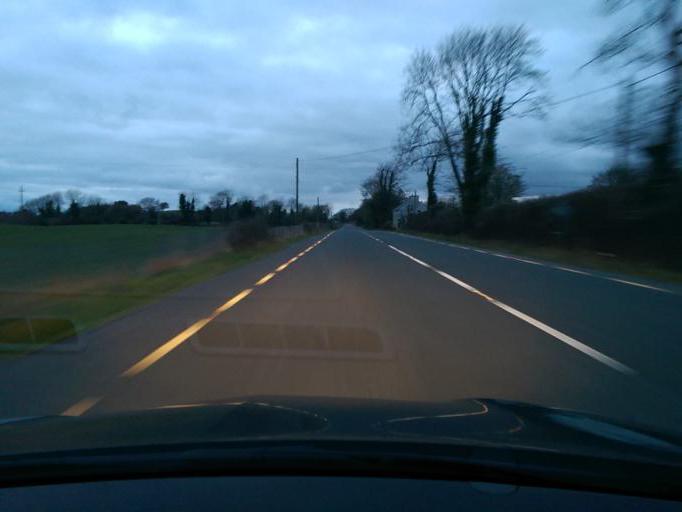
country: IE
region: Connaught
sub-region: County Galway
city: Portumna
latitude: 53.1787
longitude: -8.3424
